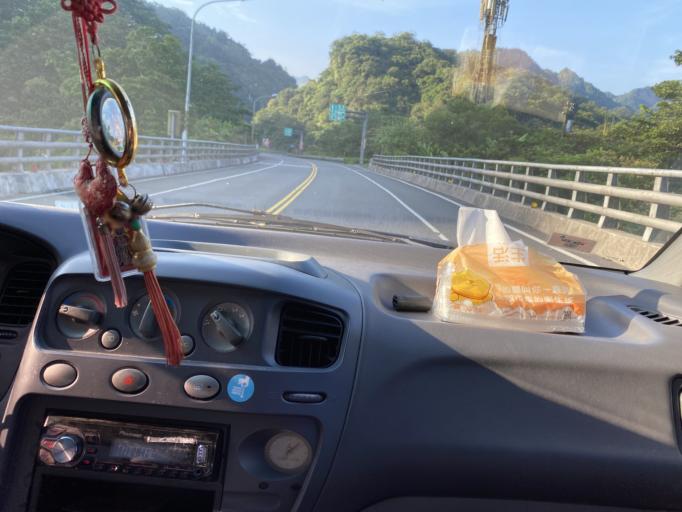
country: TW
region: Taiwan
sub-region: Keelung
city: Keelung
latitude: 25.0414
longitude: 121.7798
